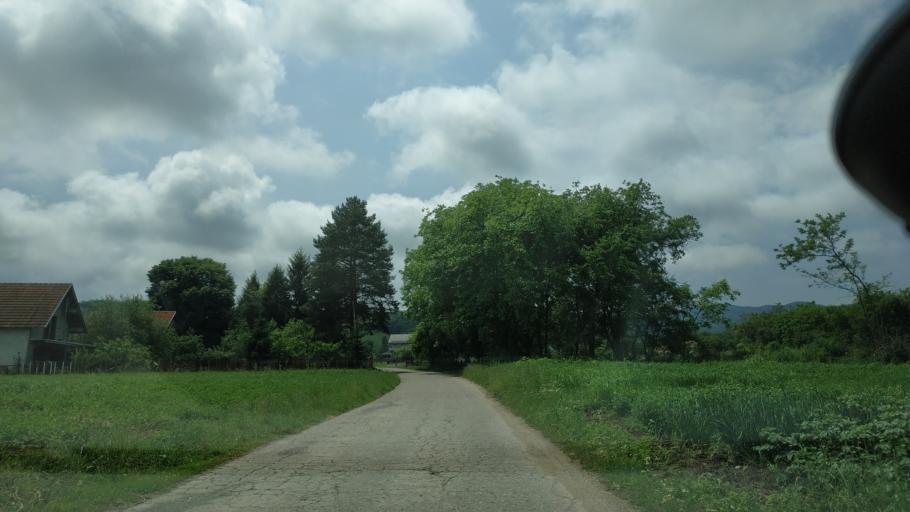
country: RS
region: Central Serbia
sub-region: Nisavski Okrug
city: Aleksinac
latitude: 43.4289
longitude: 21.7100
